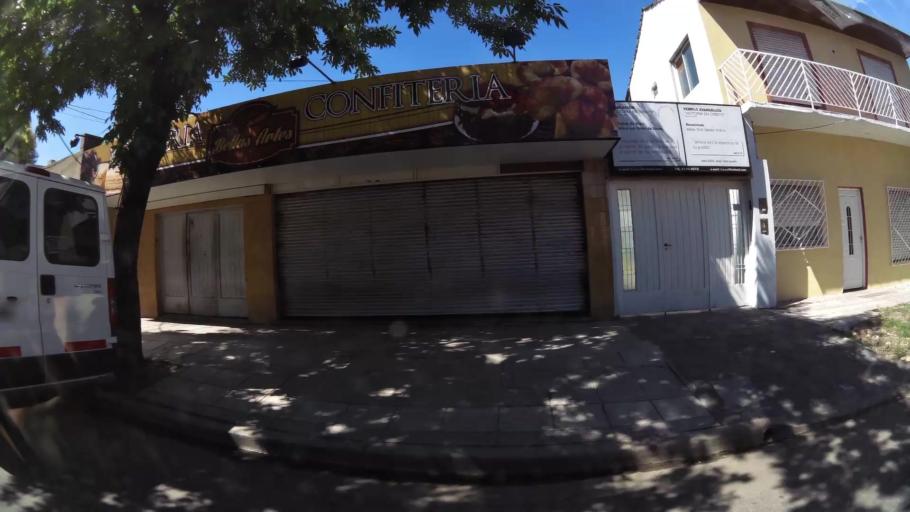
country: AR
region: Buenos Aires
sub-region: Partido de General San Martin
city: General San Martin
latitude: -34.5300
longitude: -58.5645
